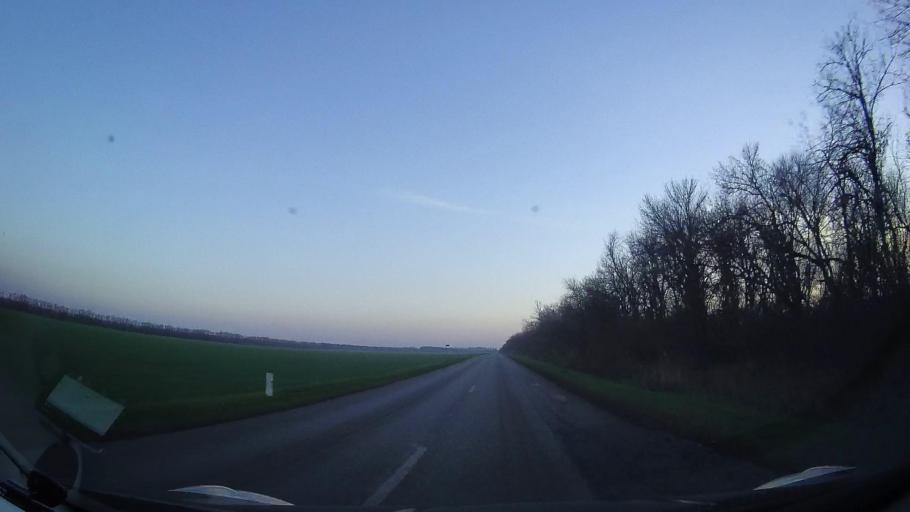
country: RU
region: Rostov
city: Zernograd
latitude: 46.9818
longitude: 40.3914
